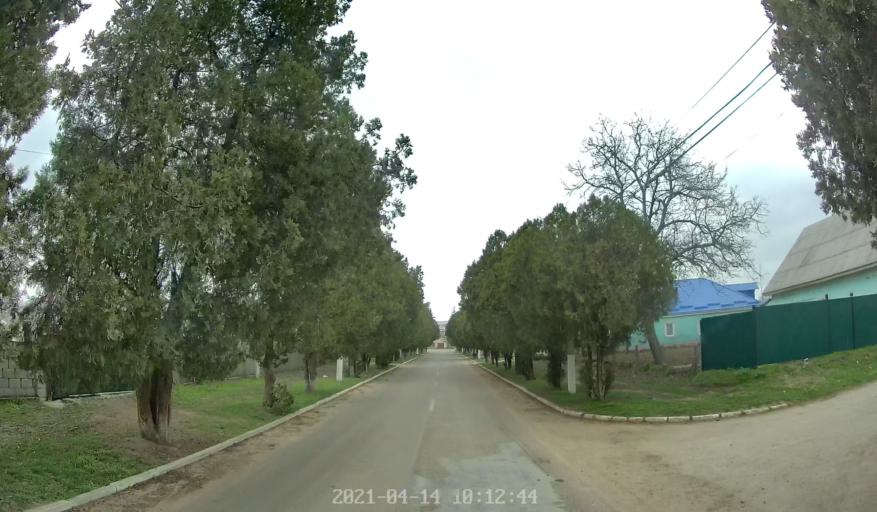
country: MD
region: Criuleni
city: Criuleni
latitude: 47.1477
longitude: 29.1318
